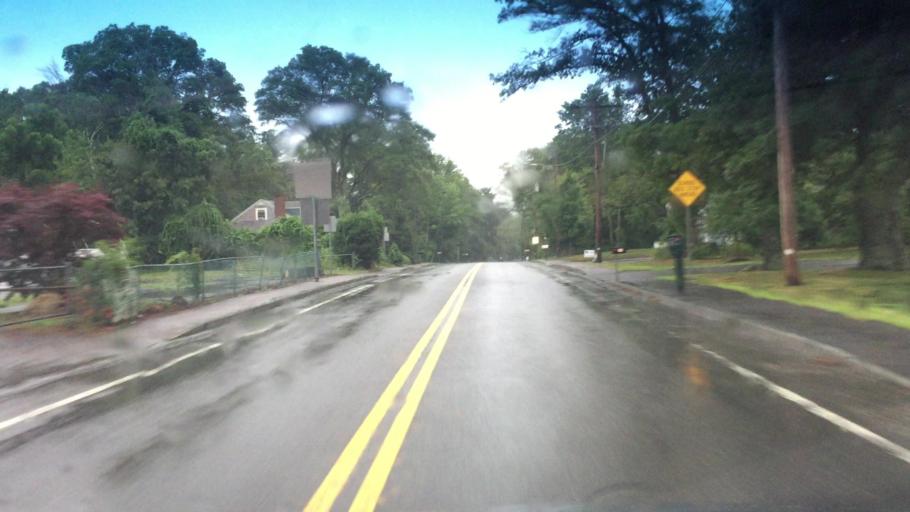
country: US
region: Massachusetts
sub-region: Norfolk County
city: Medway
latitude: 42.1443
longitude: -71.4430
